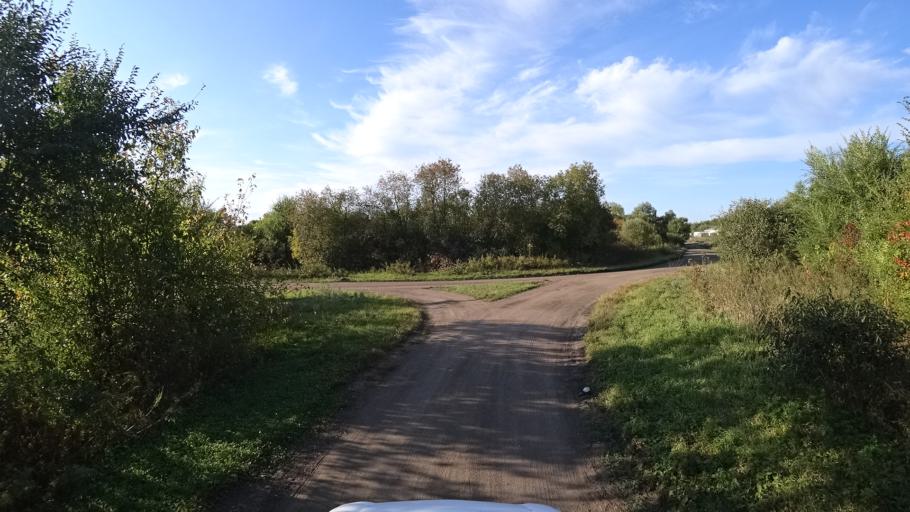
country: RU
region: Amur
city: Arkhara
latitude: 49.3554
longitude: 130.1157
